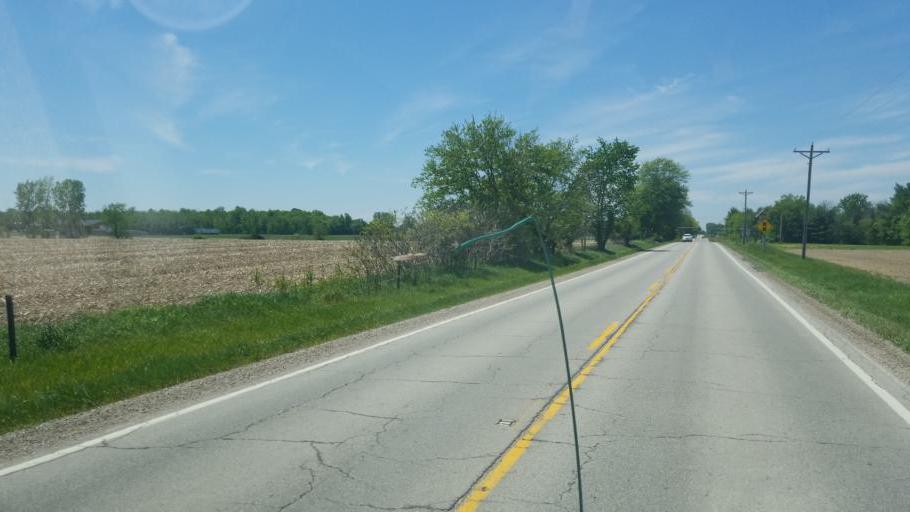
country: US
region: Ohio
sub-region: Huron County
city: Greenwich
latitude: 41.0295
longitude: -82.4816
